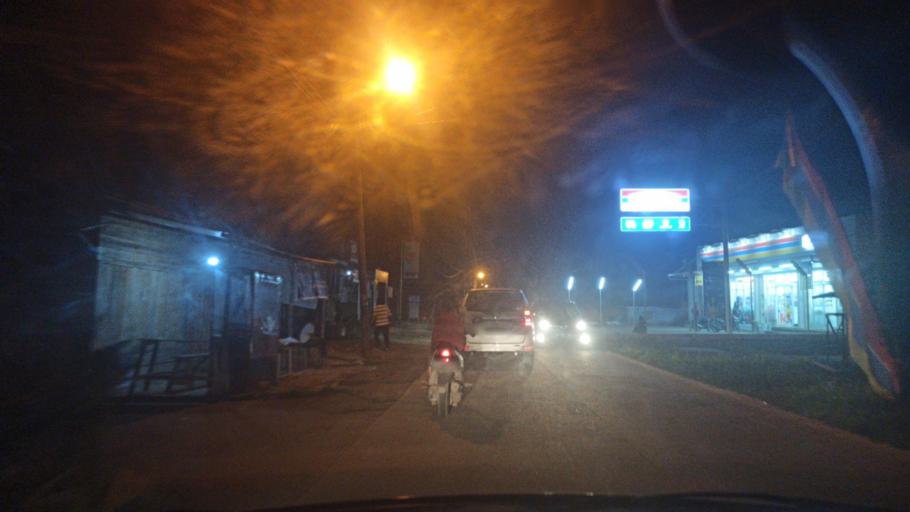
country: ID
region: South Sumatra
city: Palembang
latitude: -2.9206
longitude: 104.7963
